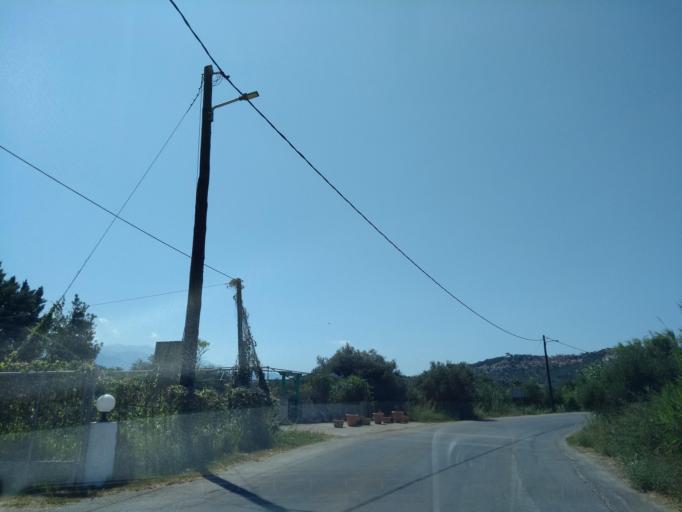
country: GR
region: Crete
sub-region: Nomos Chanias
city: Georgioupolis
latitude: 35.3650
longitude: 24.2576
